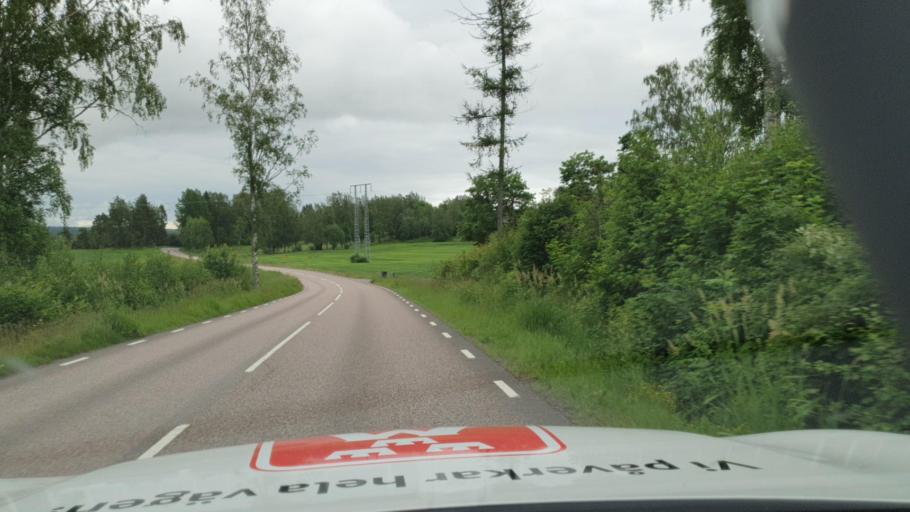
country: SE
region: Vaermland
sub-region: Kils Kommun
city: Kil
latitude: 59.5144
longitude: 13.3827
